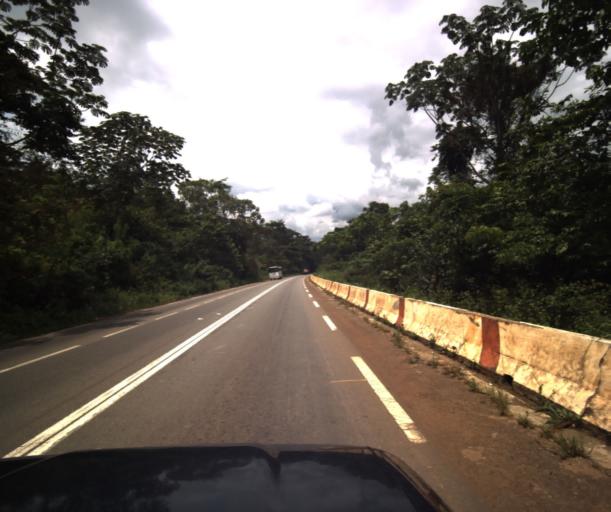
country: CM
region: Centre
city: Eseka
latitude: 3.8741
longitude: 10.8245
